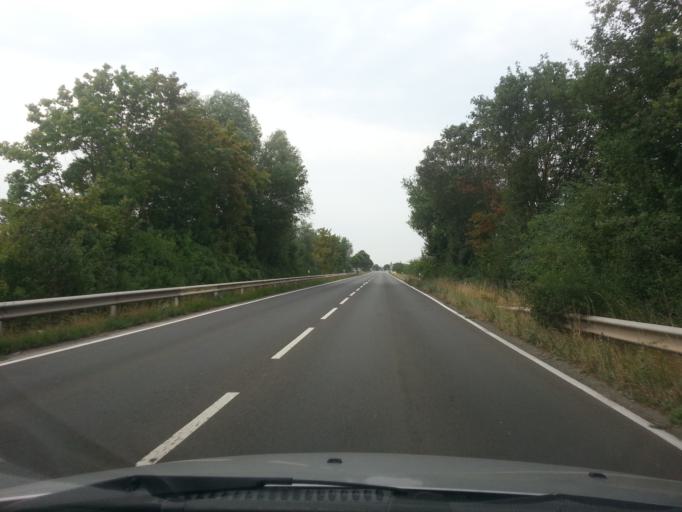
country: DE
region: Rheinland-Pfalz
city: Bobenheim-Roxheim
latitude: 49.6088
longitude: 8.3586
